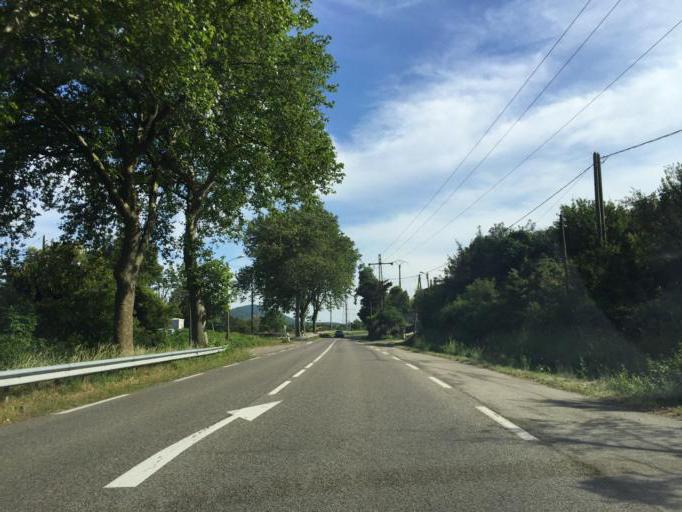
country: FR
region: Rhone-Alpes
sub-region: Departement de l'Ardeche
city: Cruas
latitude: 44.6735
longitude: 4.7703
